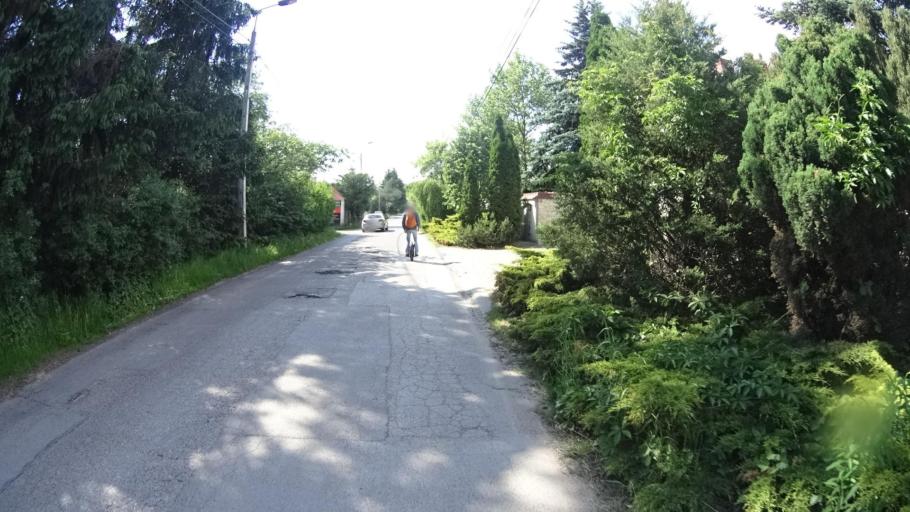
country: PL
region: Masovian Voivodeship
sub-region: Powiat piaseczynski
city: Jozefoslaw
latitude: 52.1121
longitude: 21.0354
